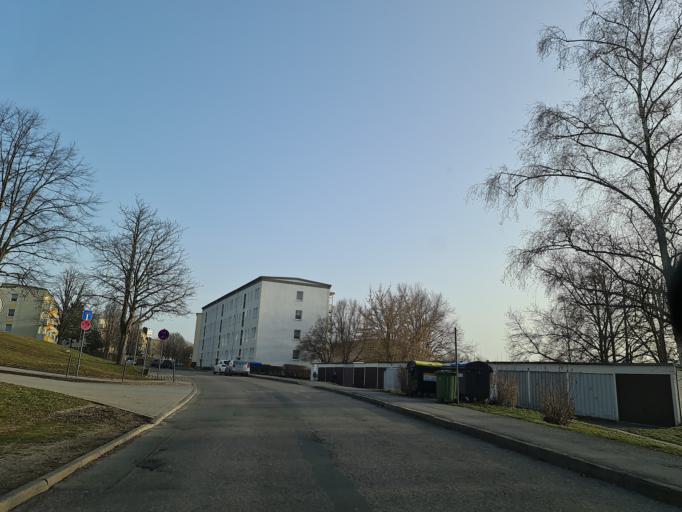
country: DE
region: Thuringia
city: Gera
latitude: 50.8981
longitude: 12.0895
